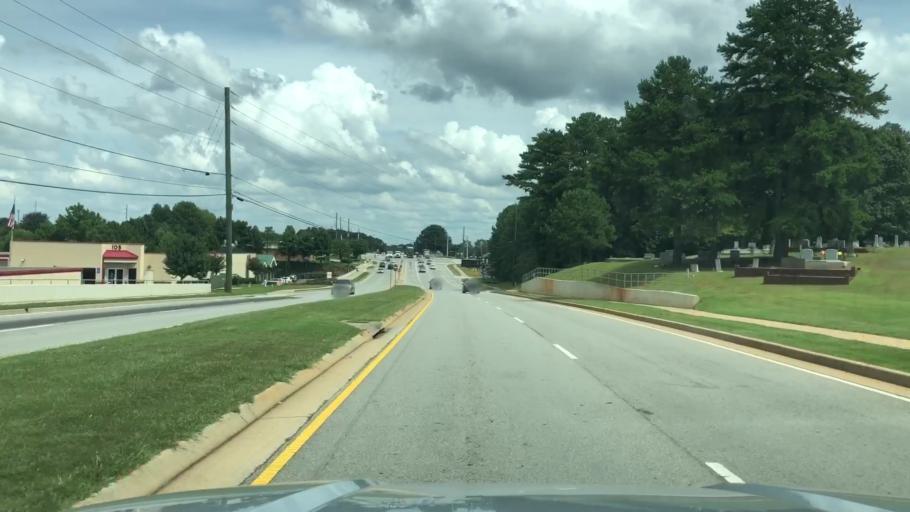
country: US
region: Georgia
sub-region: Gwinnett County
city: Suwanee
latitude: 34.0249
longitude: -84.0482
